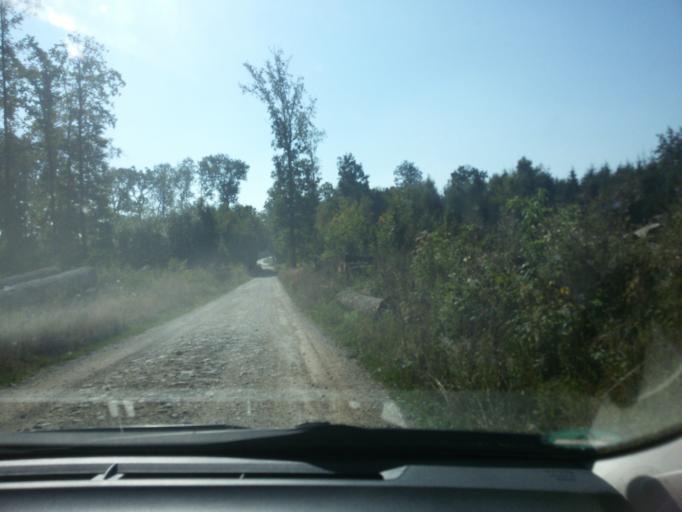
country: DE
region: Bavaria
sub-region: Swabia
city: Hainsfarth
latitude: 48.9876
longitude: 10.5835
